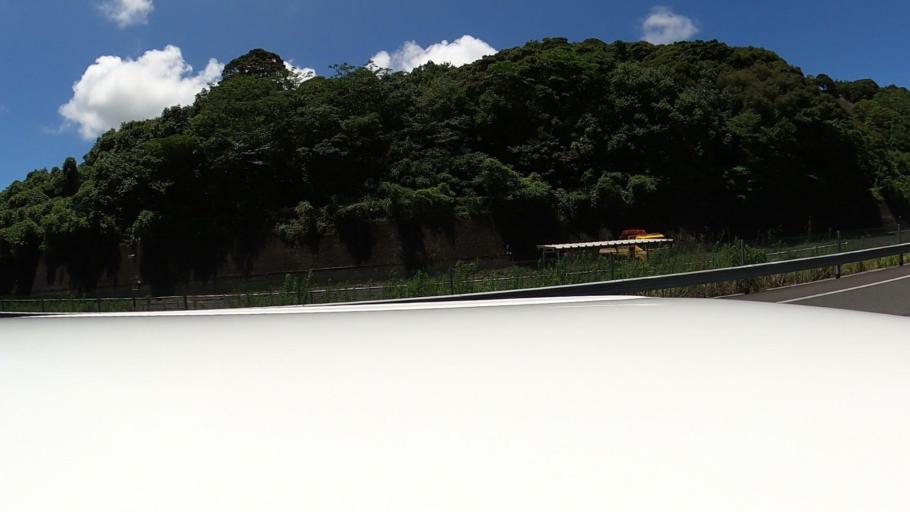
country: JP
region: Miyazaki
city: Nobeoka
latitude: 32.5044
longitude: 131.6624
